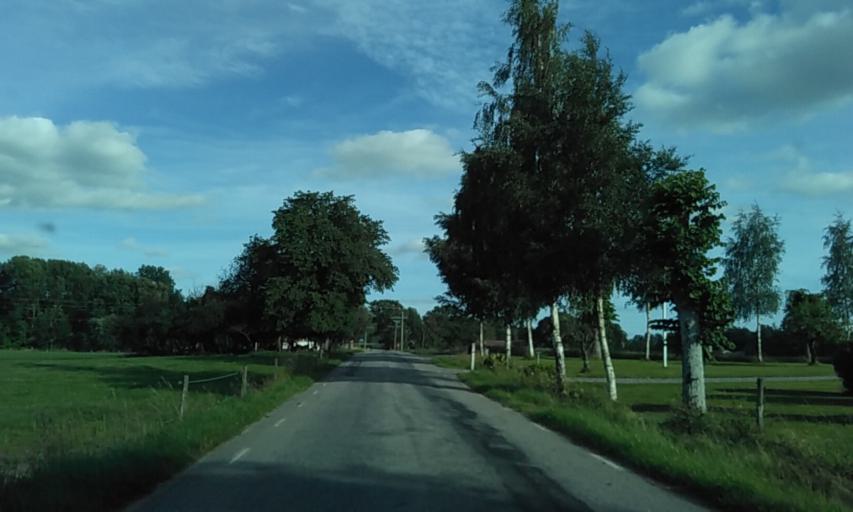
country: SE
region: Vaestra Goetaland
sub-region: Vara Kommun
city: Vara
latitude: 58.3644
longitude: 12.8618
